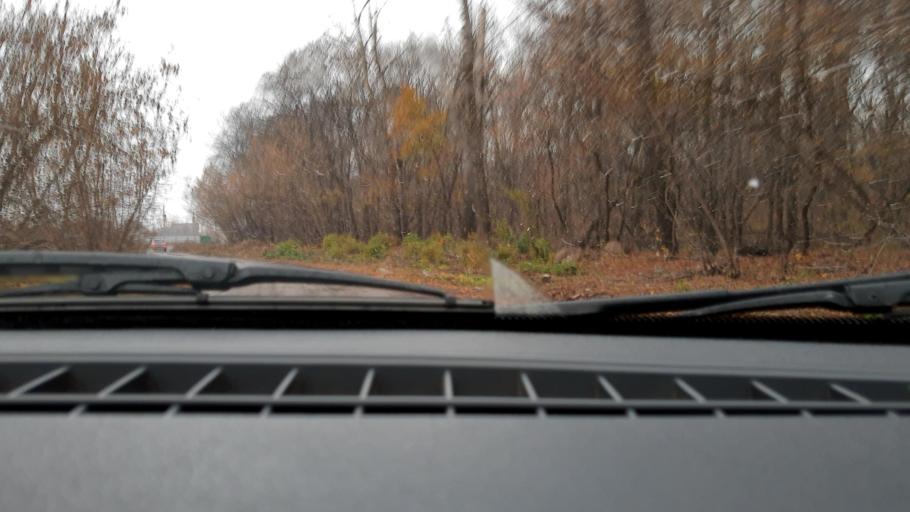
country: RU
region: Bashkortostan
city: Ufa
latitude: 54.7589
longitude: 55.9215
